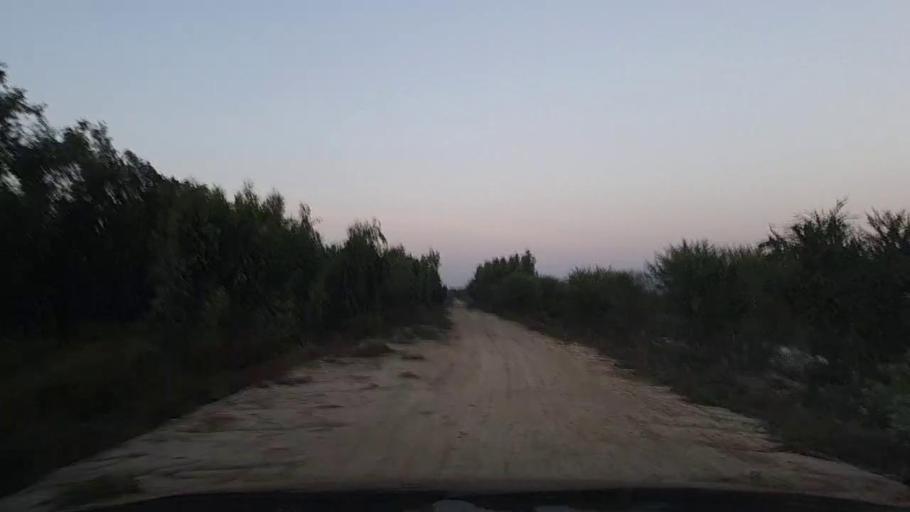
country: PK
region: Sindh
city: Thatta
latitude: 24.7420
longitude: 67.9570
